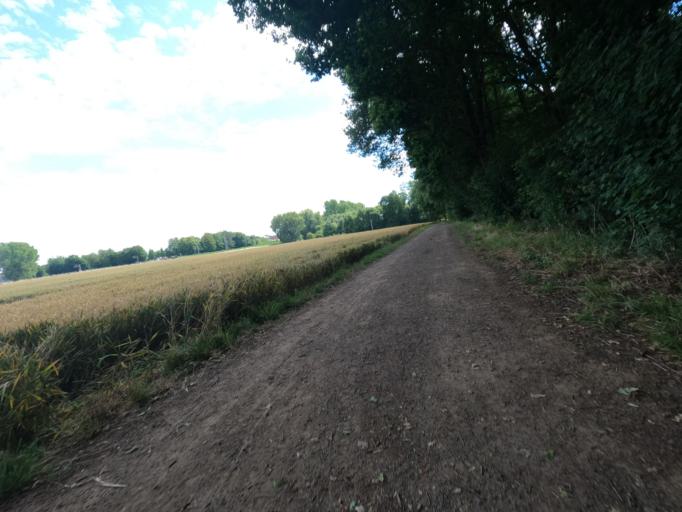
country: DE
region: North Rhine-Westphalia
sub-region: Regierungsbezirk Koln
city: Heinsberg
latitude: 51.0501
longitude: 6.1466
